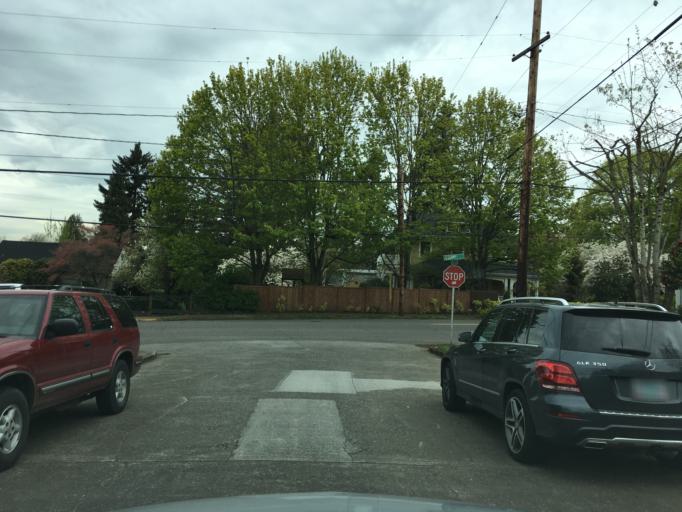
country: US
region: Oregon
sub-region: Multnomah County
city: Lents
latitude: 45.5227
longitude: -122.5976
